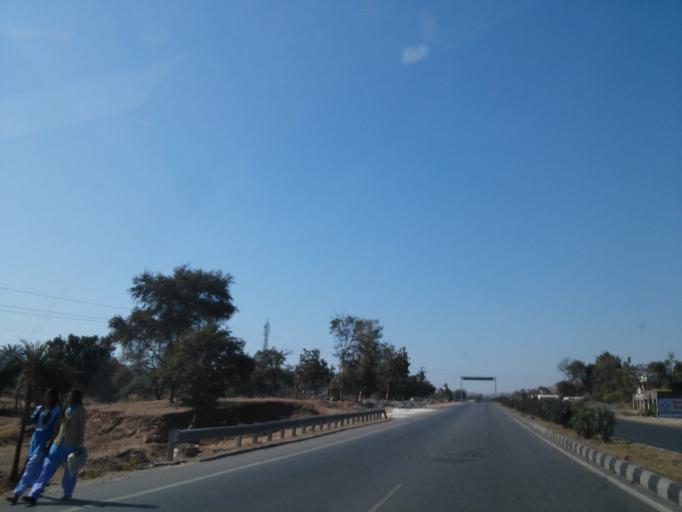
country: IN
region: Rajasthan
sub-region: Dungarpur
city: Dungarpur
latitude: 24.0004
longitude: 73.6433
